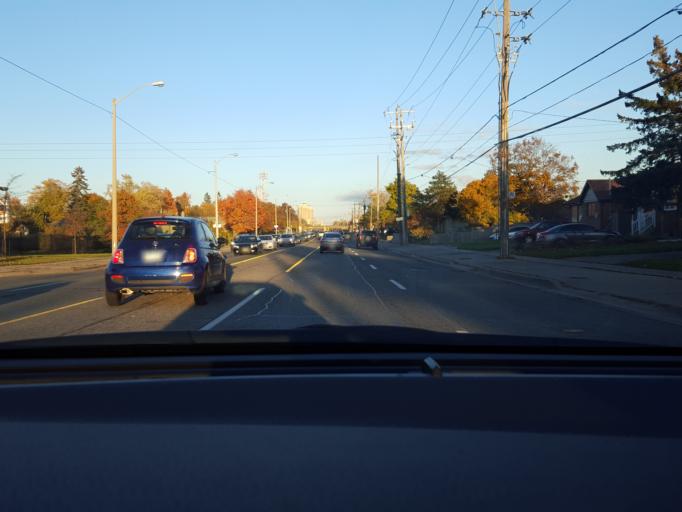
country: CA
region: Ontario
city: Scarborough
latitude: 43.7598
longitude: -79.3067
